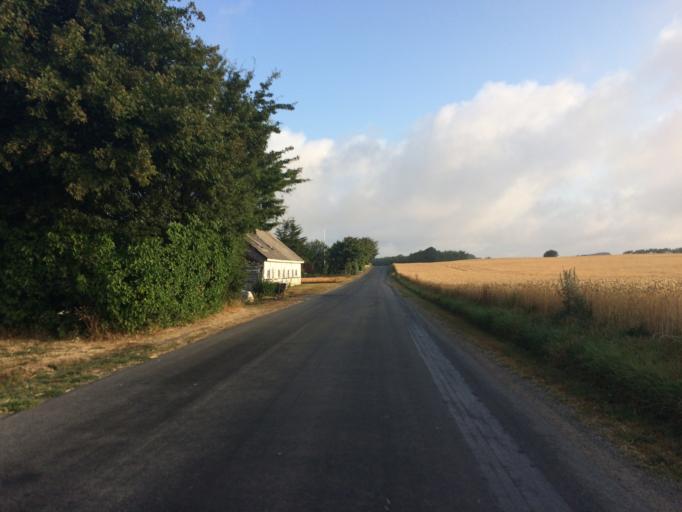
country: DK
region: Central Jutland
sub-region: Holstebro Kommune
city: Vinderup
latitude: 56.5835
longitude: 8.7569
